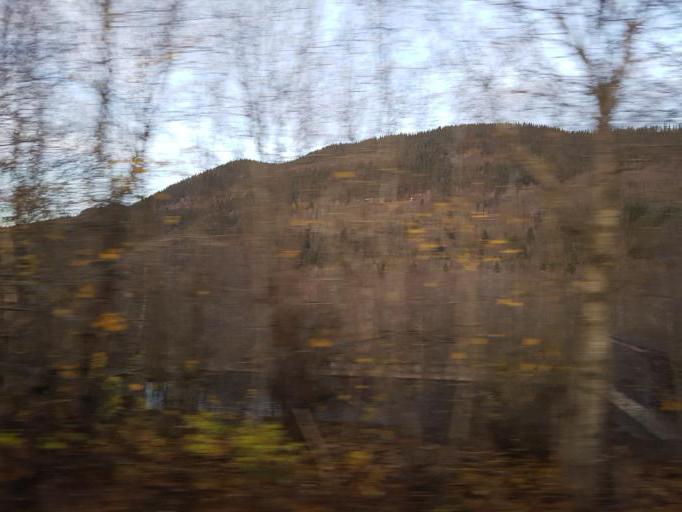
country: NO
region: Sor-Trondelag
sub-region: Melhus
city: Lundamo
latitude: 63.1587
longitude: 10.2925
